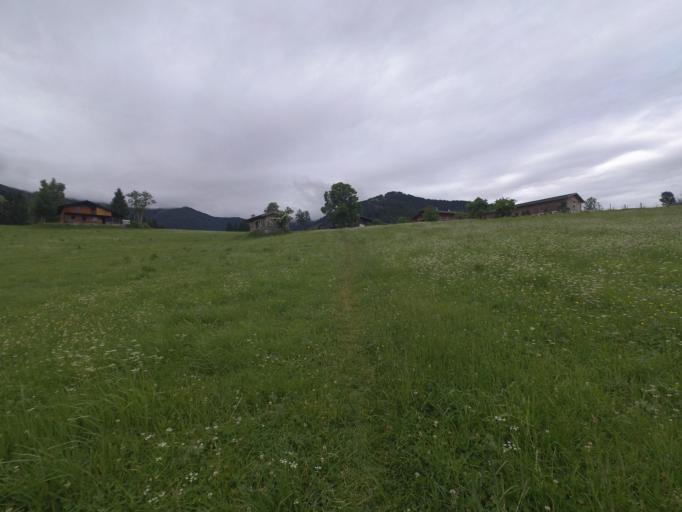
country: AT
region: Salzburg
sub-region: Politischer Bezirk Zell am See
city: Leogang
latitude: 47.4333
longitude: 12.7510
